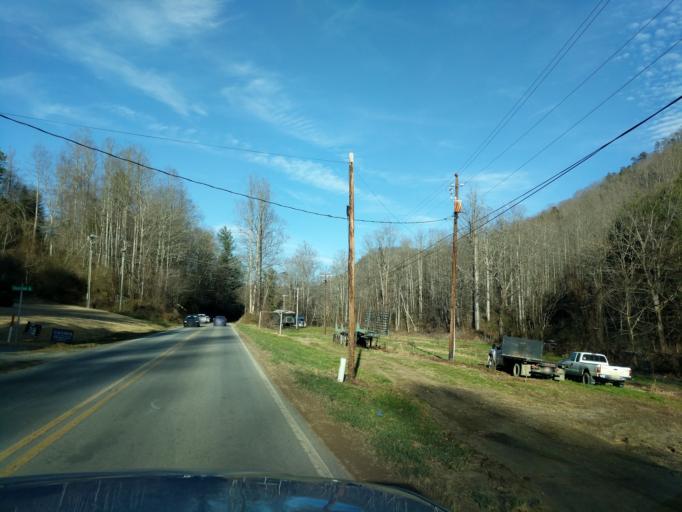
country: US
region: North Carolina
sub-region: Henderson County
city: Edneyville
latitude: 35.4202
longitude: -82.3104
